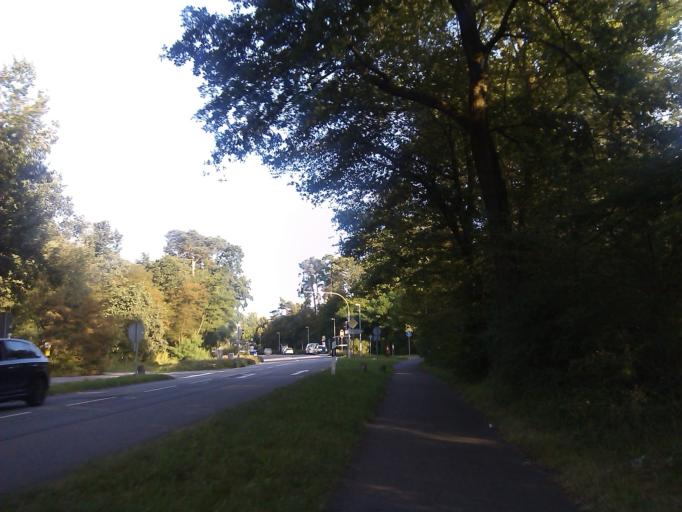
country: DE
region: Baden-Wuerttemberg
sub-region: Karlsruhe Region
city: Walldorf
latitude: 49.3164
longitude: 8.6343
